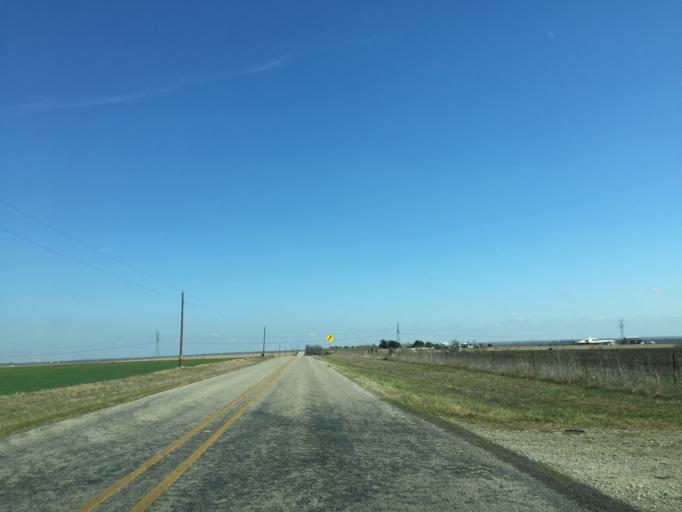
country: US
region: Texas
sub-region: Williamson County
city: Granger
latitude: 30.7573
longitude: -97.5333
